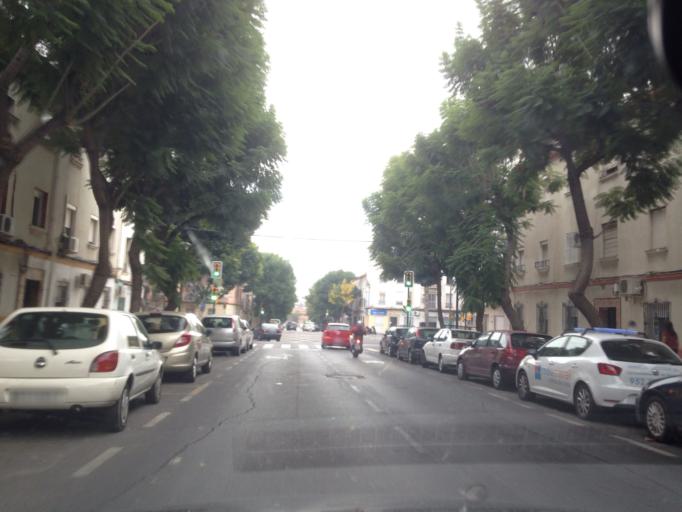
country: ES
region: Andalusia
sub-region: Provincia de Malaga
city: Malaga
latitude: 36.7163
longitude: -4.4457
